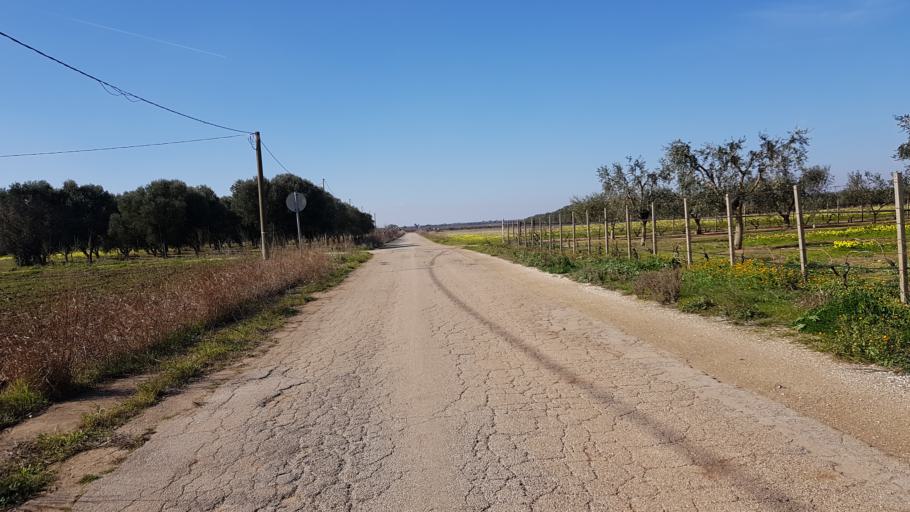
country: IT
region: Apulia
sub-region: Provincia di Brindisi
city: Mesagne
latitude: 40.6205
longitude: 17.7895
